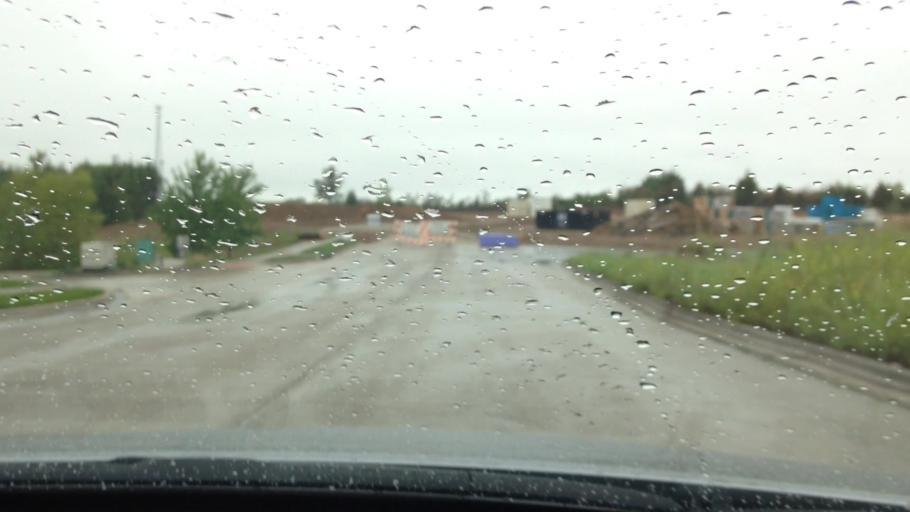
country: US
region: Kansas
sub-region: Wyandotte County
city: Bonner Springs
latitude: 39.0982
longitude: -94.8853
